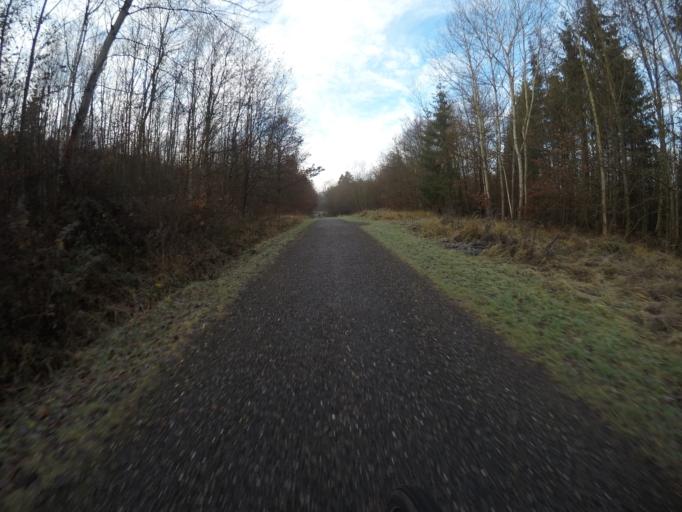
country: DE
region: Baden-Wuerttemberg
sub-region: Regierungsbezirk Stuttgart
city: Sindelfingen
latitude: 48.7229
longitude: 9.0266
